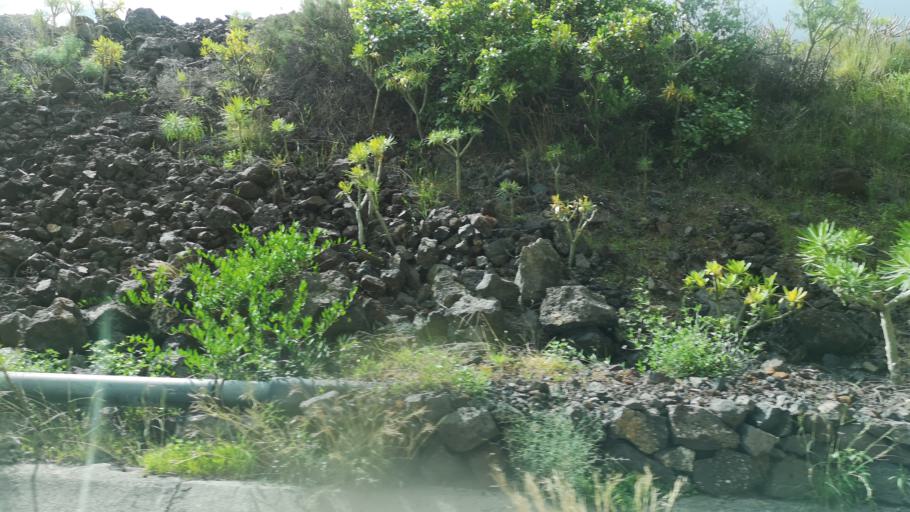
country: ES
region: Canary Islands
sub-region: Provincia de Santa Cruz de Tenerife
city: San Sebastian de la Gomera
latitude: 28.1132
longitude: -17.1351
